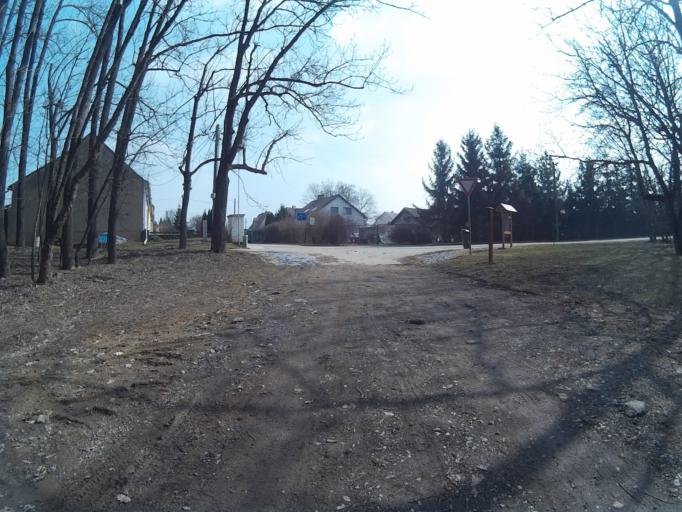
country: CZ
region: South Moravian
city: Pozorice
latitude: 49.2209
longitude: 16.7942
